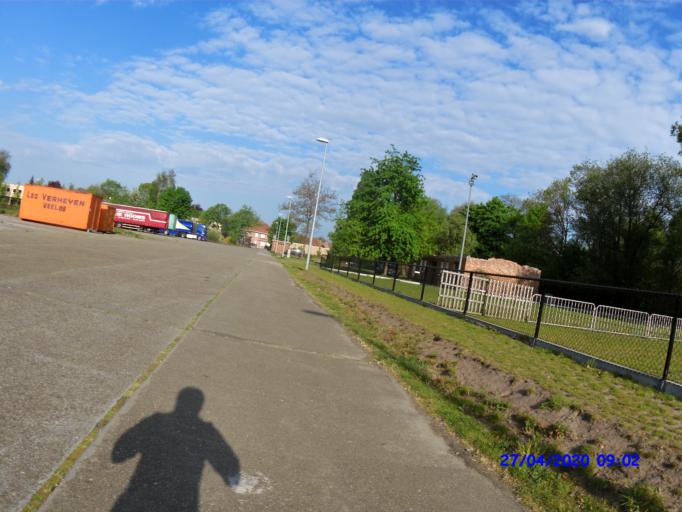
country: BE
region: Flanders
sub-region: Provincie Antwerpen
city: Turnhout
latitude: 51.3091
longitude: 4.9264
